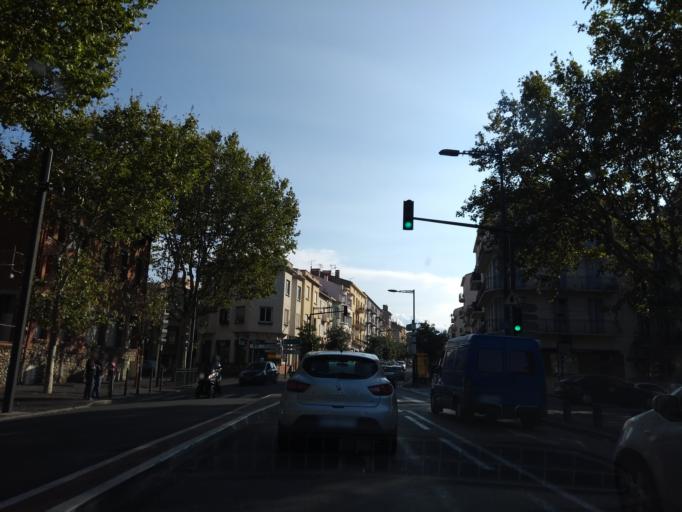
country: FR
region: Languedoc-Roussillon
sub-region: Departement des Pyrenees-Orientales
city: Perpignan
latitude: 42.6969
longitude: 2.9036
